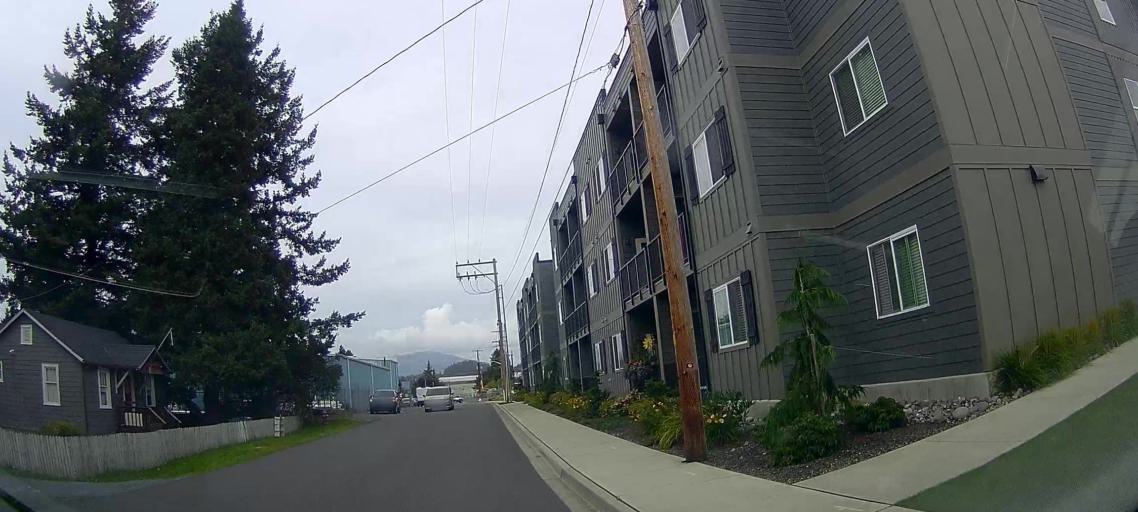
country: US
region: Washington
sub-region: Skagit County
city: Sedro-Woolley
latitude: 48.5018
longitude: -122.2420
